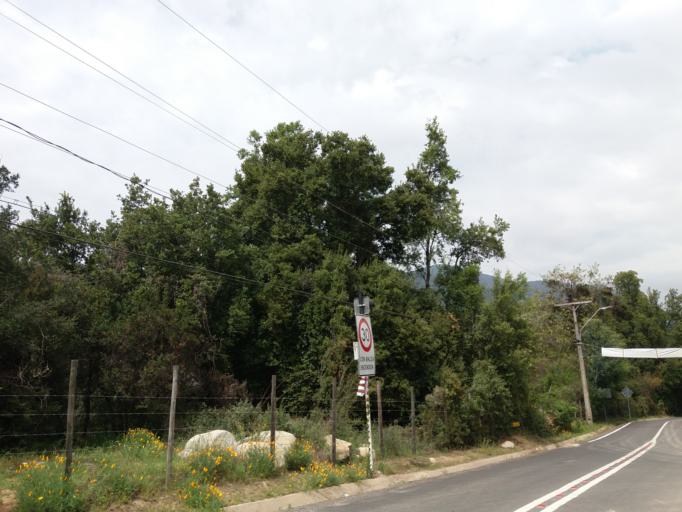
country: CL
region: Valparaiso
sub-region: Provincia de Marga Marga
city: Limache
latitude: -33.0236
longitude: -71.0732
